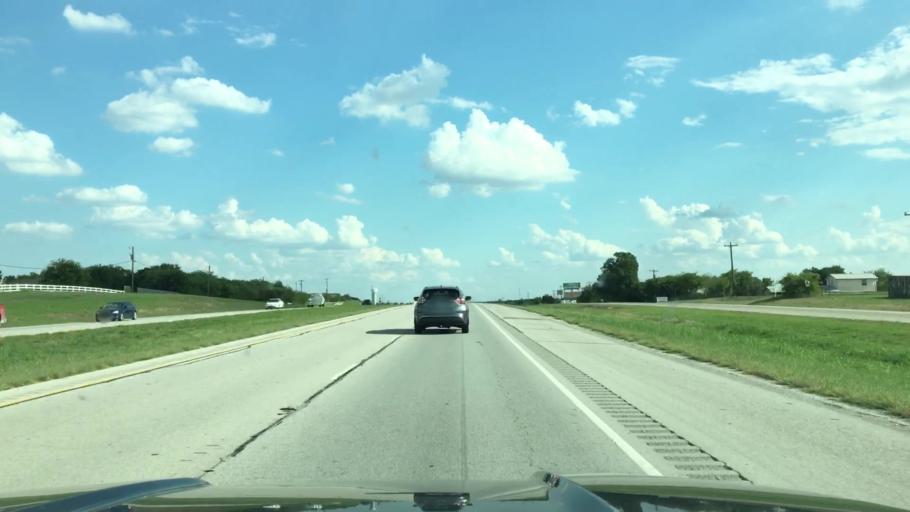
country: US
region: Texas
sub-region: Tarrant County
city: Pecan Acres
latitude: 32.9879
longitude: -97.4291
